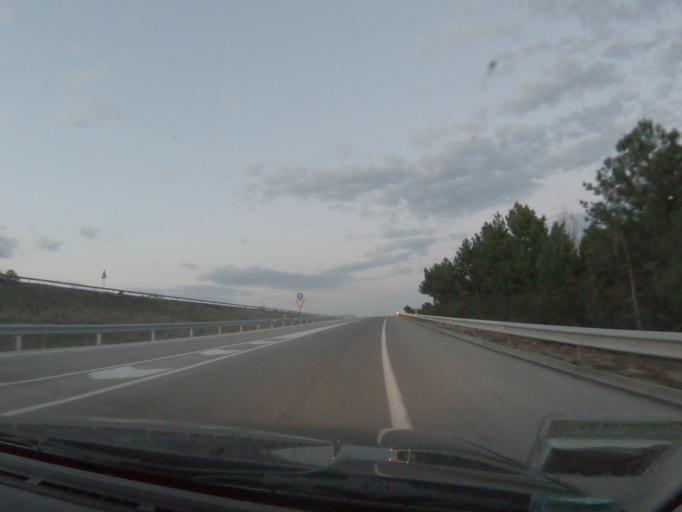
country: ES
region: Castille and Leon
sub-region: Provincia de Leon
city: Molinaseca
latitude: 42.5613
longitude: -6.5541
